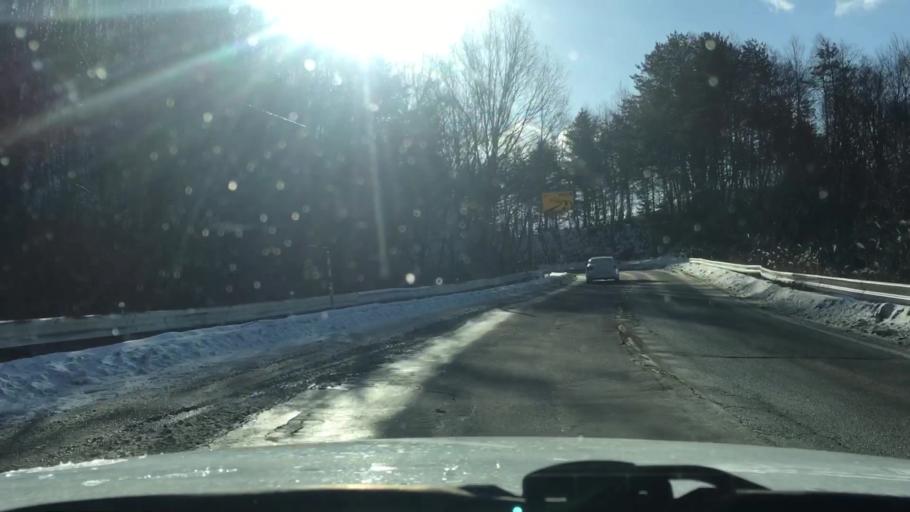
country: JP
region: Iwate
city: Morioka-shi
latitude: 39.6626
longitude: 141.3320
